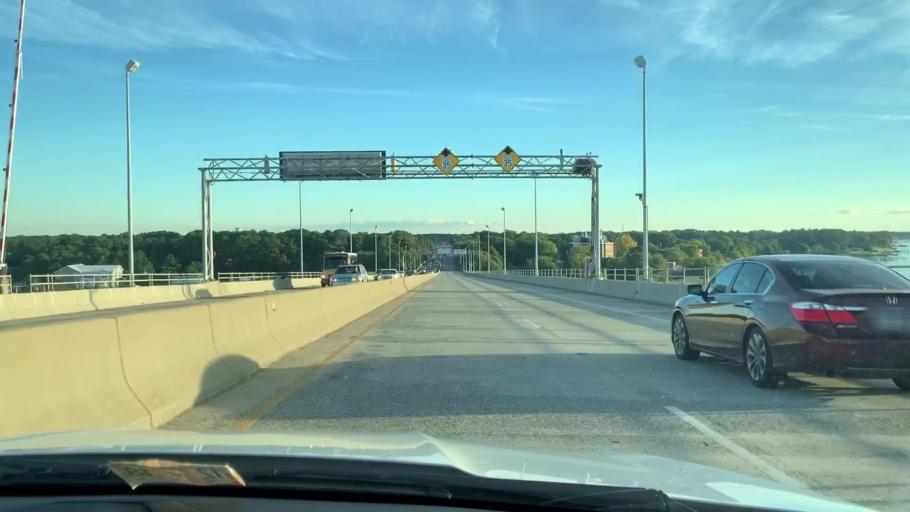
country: US
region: Virginia
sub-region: York County
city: Yorktown
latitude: 37.2447
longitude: -76.5051
